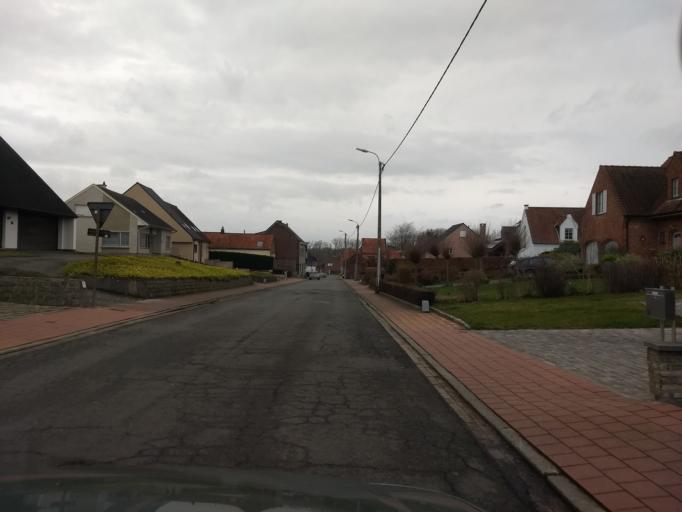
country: BE
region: Flanders
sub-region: Provincie Vlaams-Brabant
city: Liedekerke
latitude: 50.8567
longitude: 4.0726
